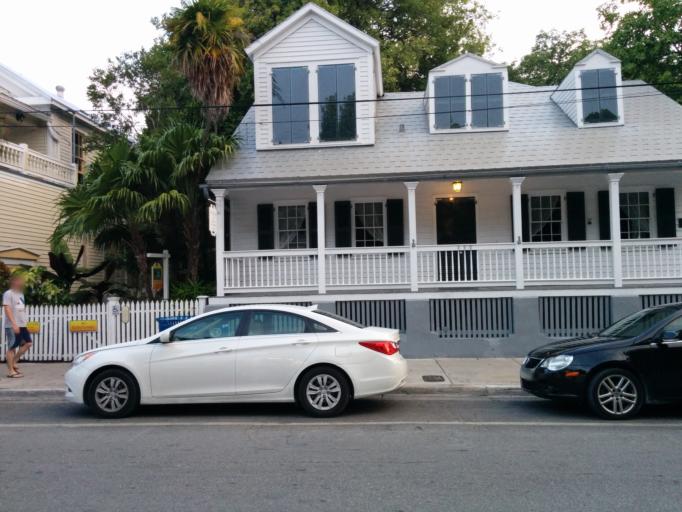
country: US
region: Florida
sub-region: Monroe County
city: Key West
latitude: 24.5575
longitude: -81.8041
